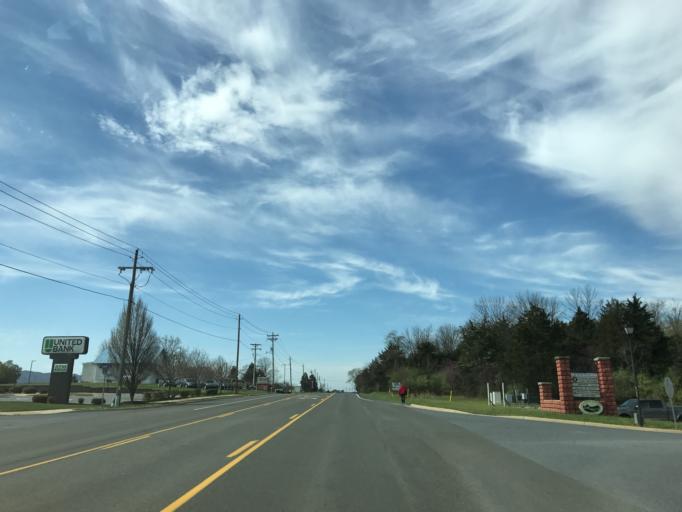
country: US
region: Virginia
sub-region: Shenandoah County
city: Strasburg
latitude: 39.0032
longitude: -78.3420
